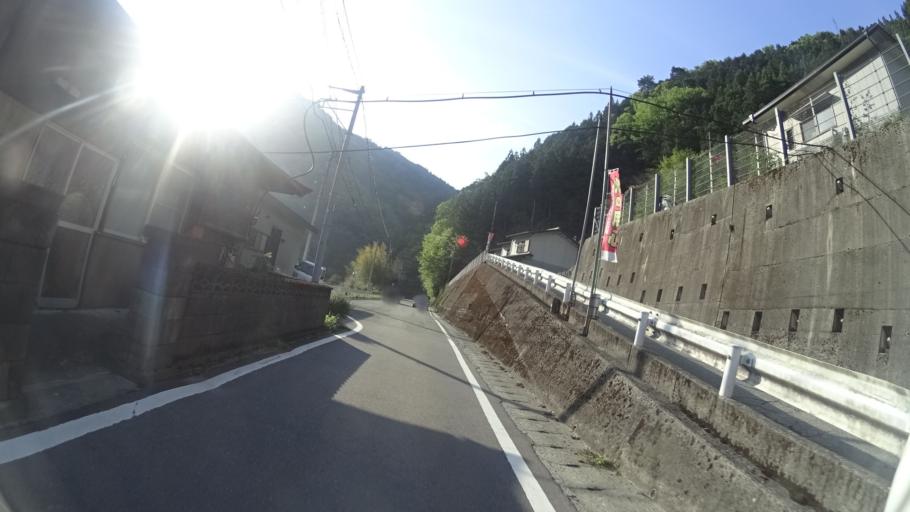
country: JP
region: Tokushima
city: Ikedacho
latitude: 33.8713
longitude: 133.8722
